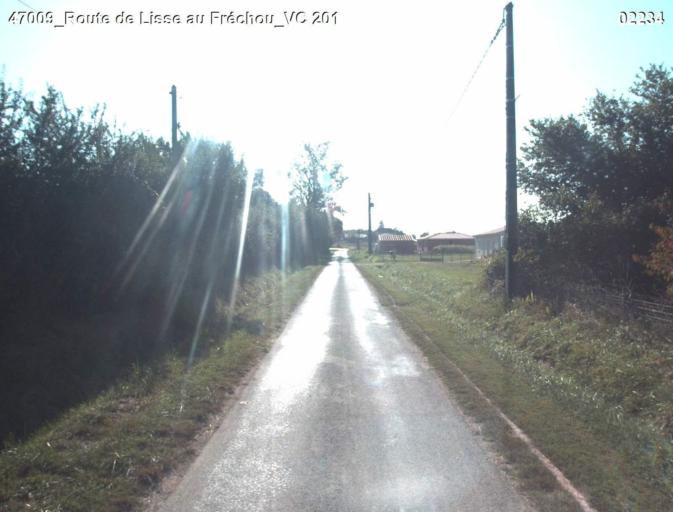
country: FR
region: Aquitaine
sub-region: Departement du Lot-et-Garonne
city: Mezin
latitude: 44.0948
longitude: 0.2853
